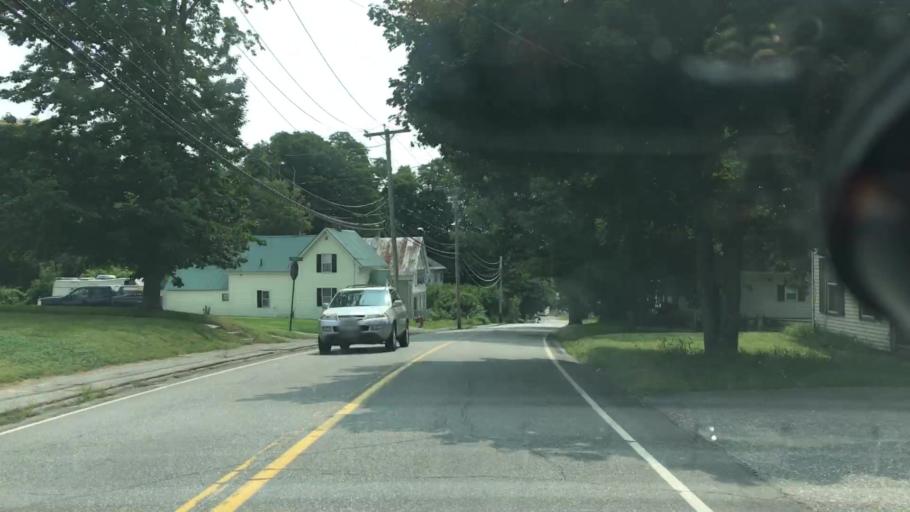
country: US
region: Maine
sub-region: Androscoggin County
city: Livermore Falls
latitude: 44.4748
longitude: -70.1874
